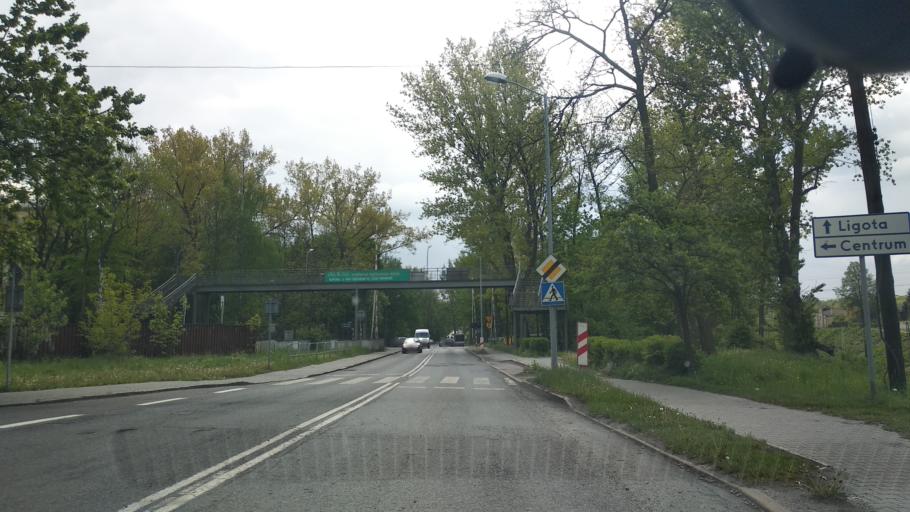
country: PL
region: Silesian Voivodeship
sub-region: Katowice
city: Katowice
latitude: 50.2435
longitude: 18.9828
